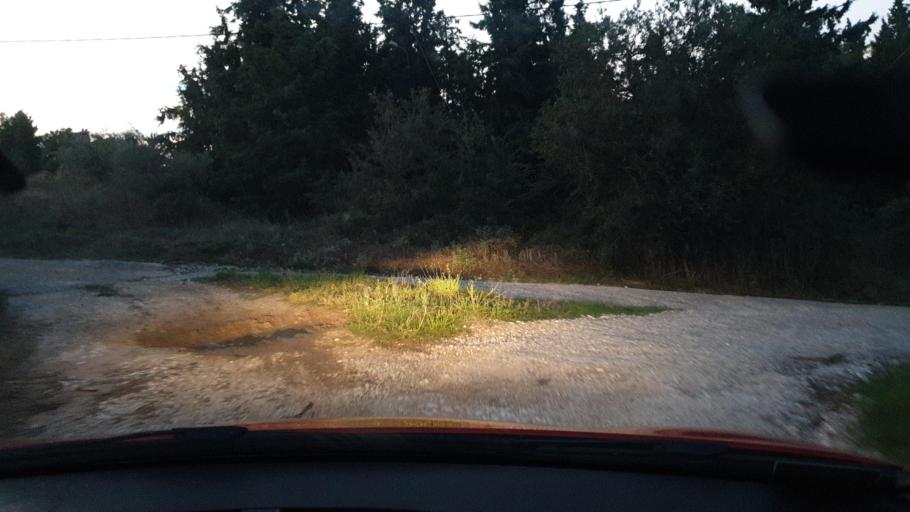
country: GR
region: Central Macedonia
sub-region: Nomos Thessalonikis
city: Agia Triada
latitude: 40.5037
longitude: 22.8352
